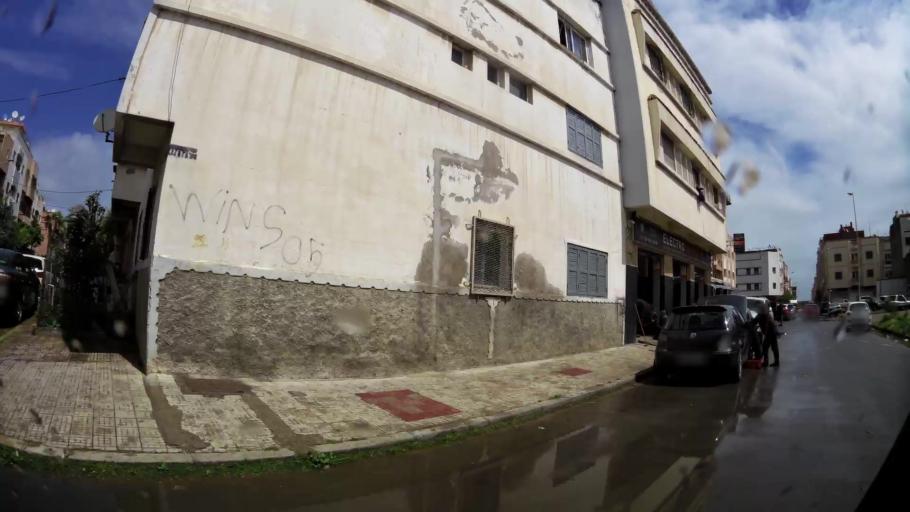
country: MA
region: Grand Casablanca
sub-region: Casablanca
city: Casablanca
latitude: 33.5504
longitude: -7.6773
